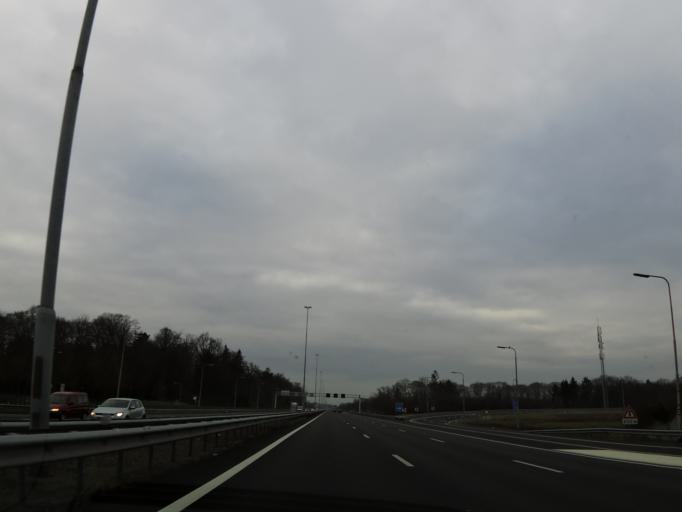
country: NL
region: North Brabant
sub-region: Gemeente Boxtel
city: Boxtel
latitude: 51.6160
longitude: 5.3176
